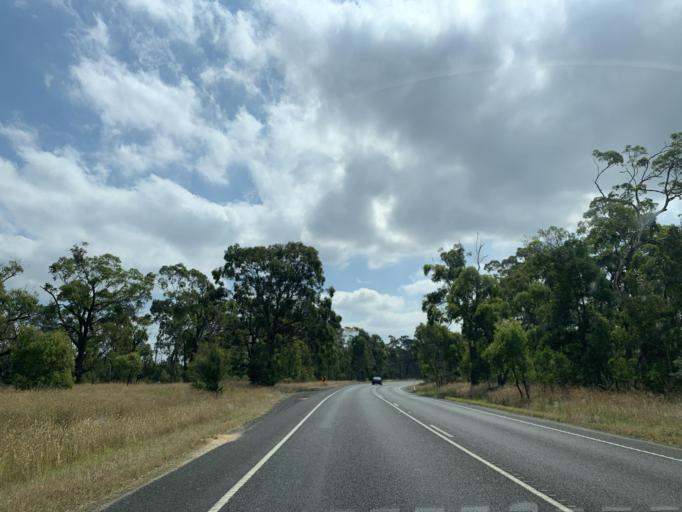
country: AU
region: Victoria
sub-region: Latrobe
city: Morwell
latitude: -38.2042
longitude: 146.4566
